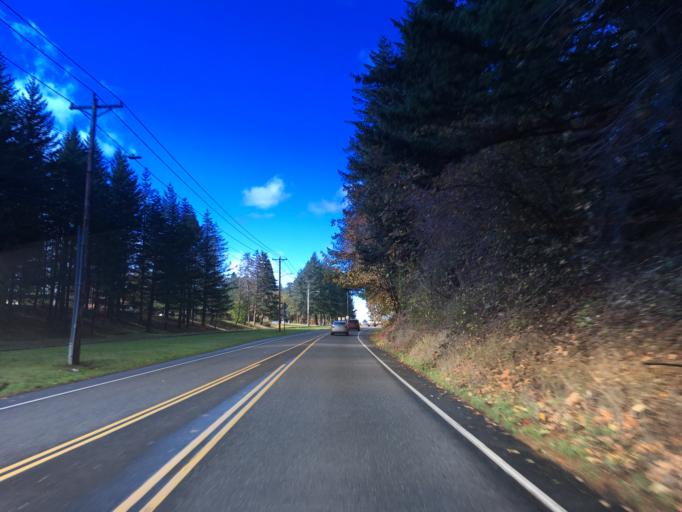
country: US
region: Oregon
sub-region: Multnomah County
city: Troutdale
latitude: 45.5189
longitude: -122.3938
